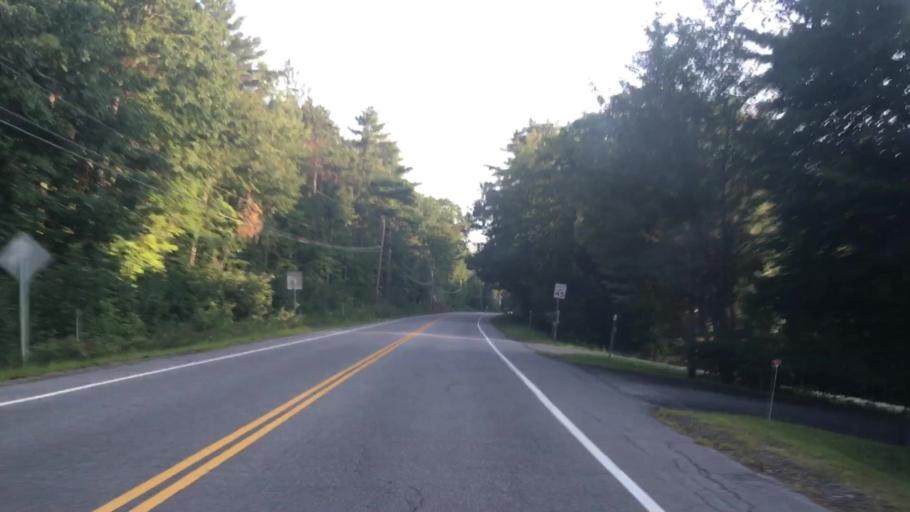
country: US
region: New Hampshire
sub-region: Belknap County
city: Gilmanton
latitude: 43.4537
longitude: -71.4212
